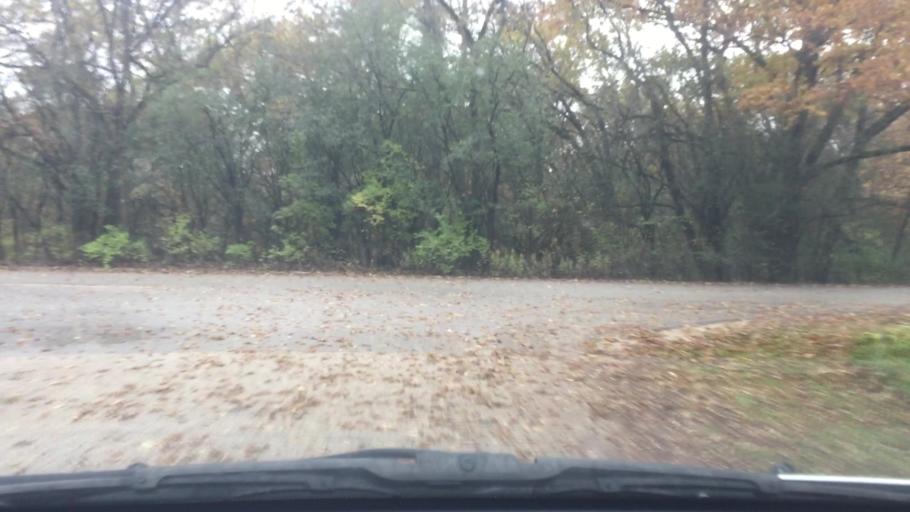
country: US
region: Wisconsin
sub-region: Waukesha County
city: North Prairie
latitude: 42.9311
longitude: -88.4525
